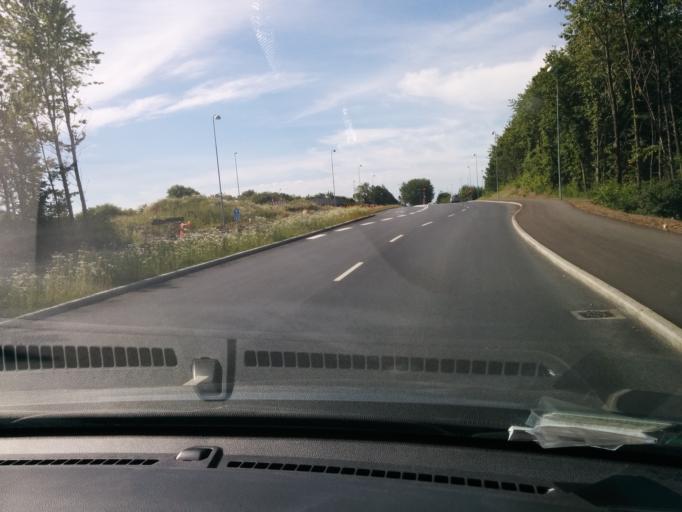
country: DK
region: Central Jutland
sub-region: Arhus Kommune
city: Arhus
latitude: 56.1847
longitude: 10.1698
